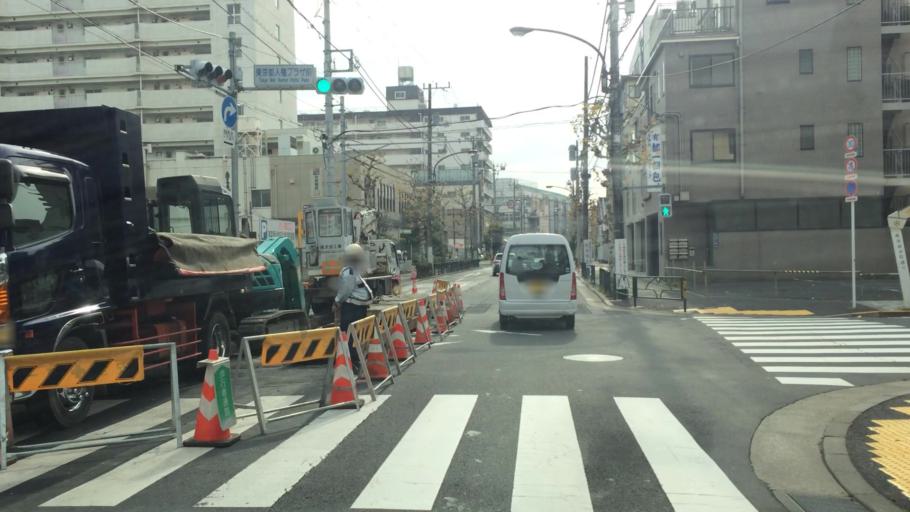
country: JP
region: Tokyo
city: Urayasu
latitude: 35.7227
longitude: 139.8073
